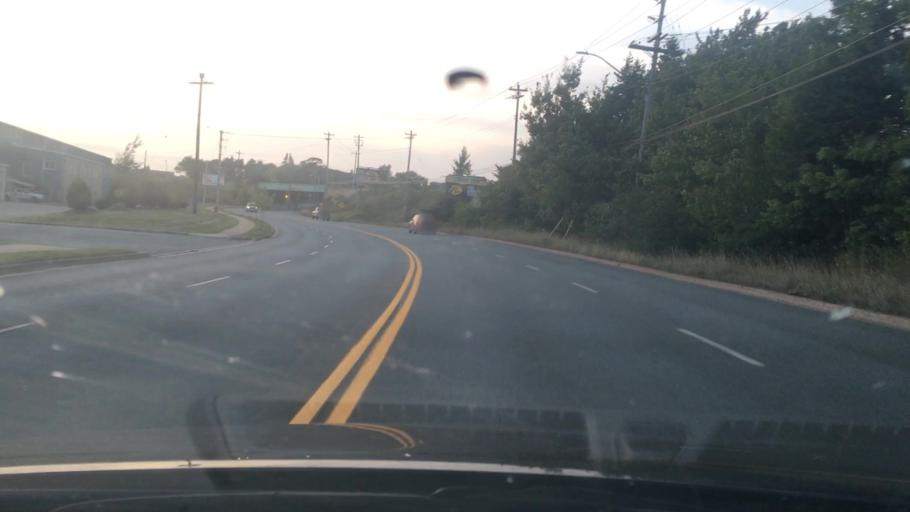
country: CA
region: Nova Scotia
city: Halifax
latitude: 44.6339
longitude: -63.5237
